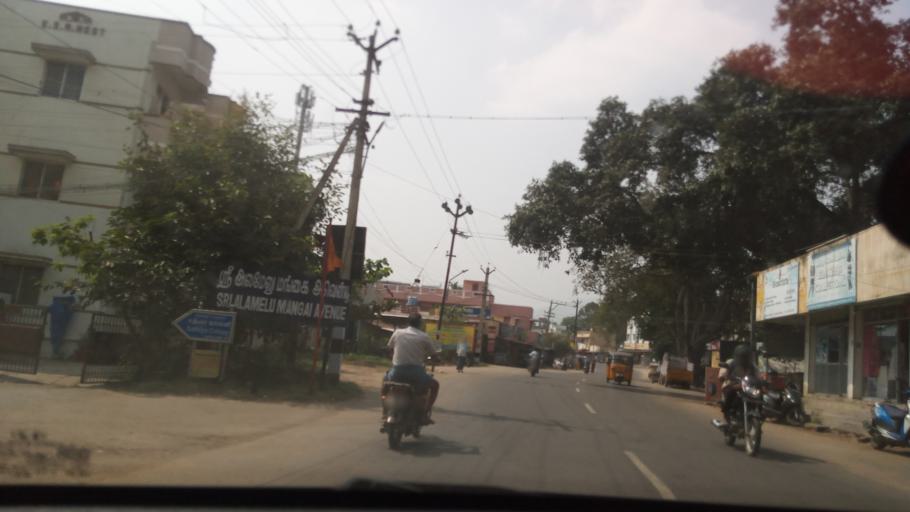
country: IN
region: Tamil Nadu
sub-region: Coimbatore
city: Perur
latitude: 11.0246
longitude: 76.9036
